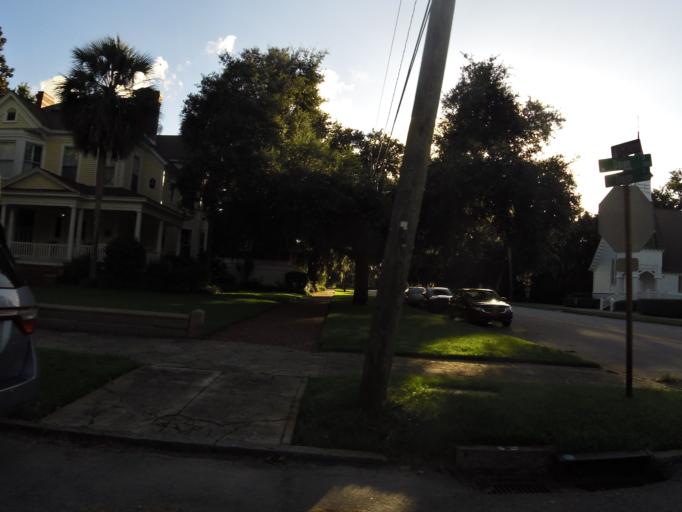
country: US
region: Georgia
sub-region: Glynn County
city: Brunswick
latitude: 31.1441
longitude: -81.4915
